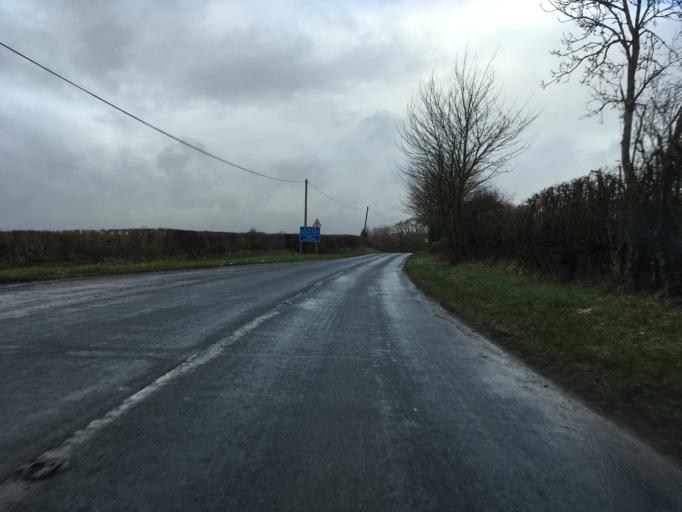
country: GB
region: England
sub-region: Gloucestershire
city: Tetbury
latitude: 51.6221
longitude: -2.1272
